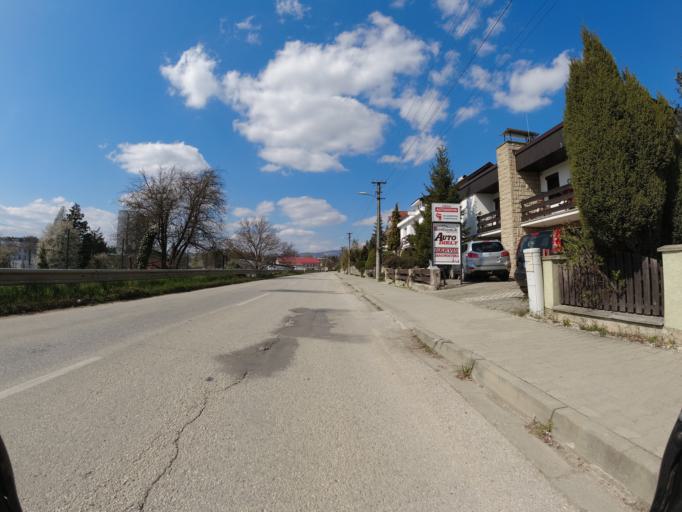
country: SK
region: Nitriansky
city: Stara Tura
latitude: 48.7717
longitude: 17.7000
